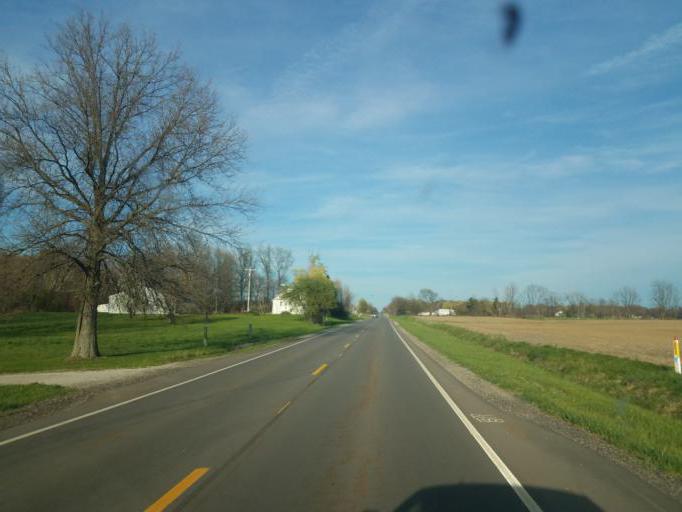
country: US
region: Ohio
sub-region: Crawford County
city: Galion
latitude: 40.6901
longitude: -82.7538
